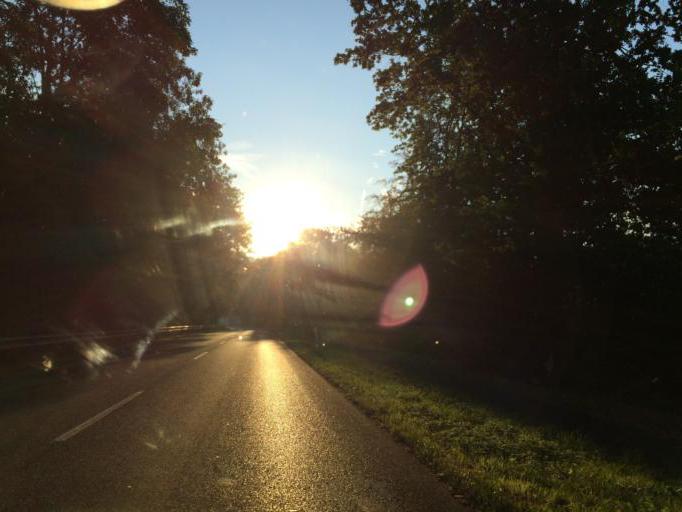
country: DE
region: North Rhine-Westphalia
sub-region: Regierungsbezirk Koln
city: Konigswinter
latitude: 50.6363
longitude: 7.1651
